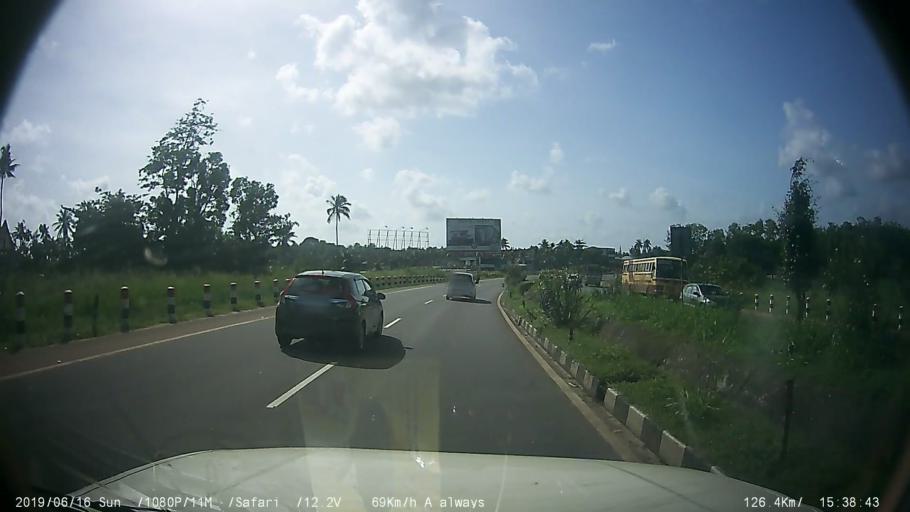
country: IN
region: Kerala
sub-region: Thrissur District
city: Irinjalakuda
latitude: 10.4130
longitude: 76.2711
